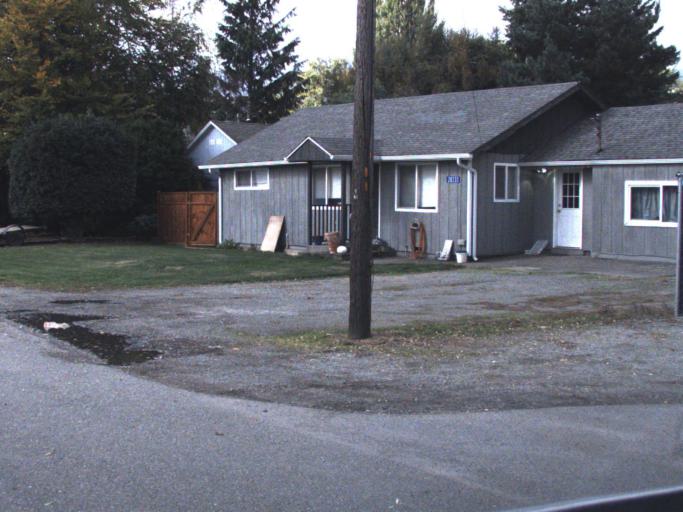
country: US
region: Washington
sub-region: Skagit County
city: Burlington
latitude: 48.4830
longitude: -122.3064
